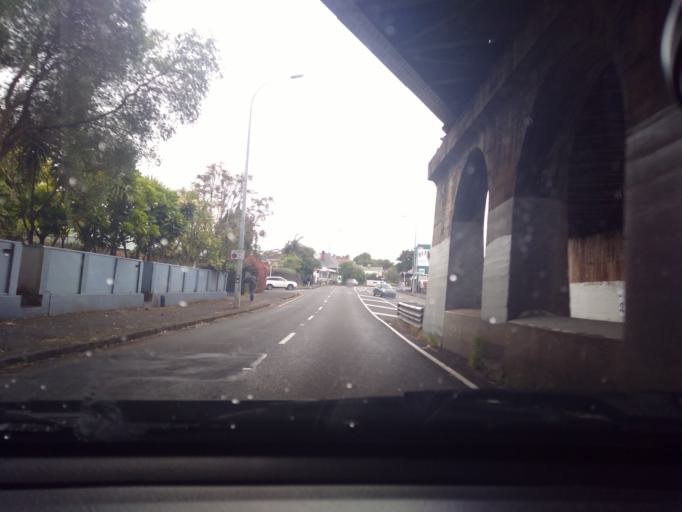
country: NZ
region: Auckland
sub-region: Auckland
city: Auckland
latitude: -36.8762
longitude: 174.7314
